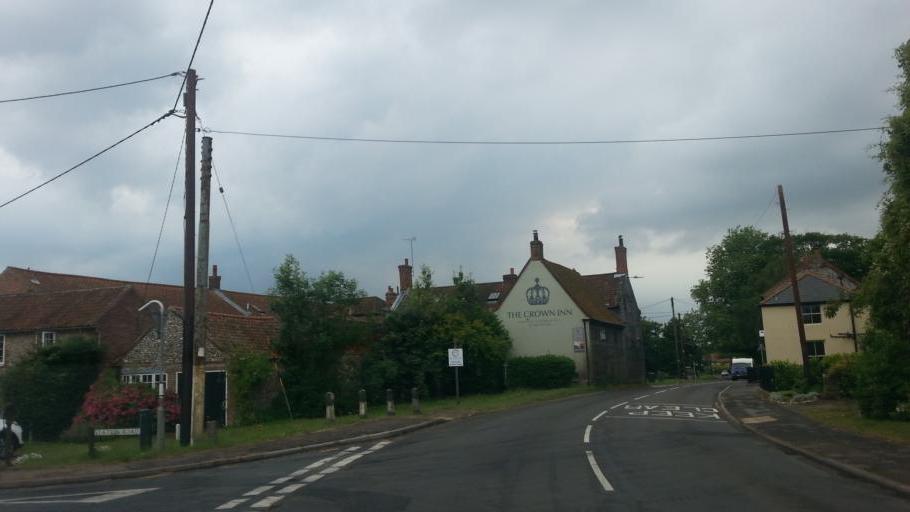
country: GB
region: England
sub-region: Norfolk
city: Fakenham
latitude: 52.8208
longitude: 0.7112
